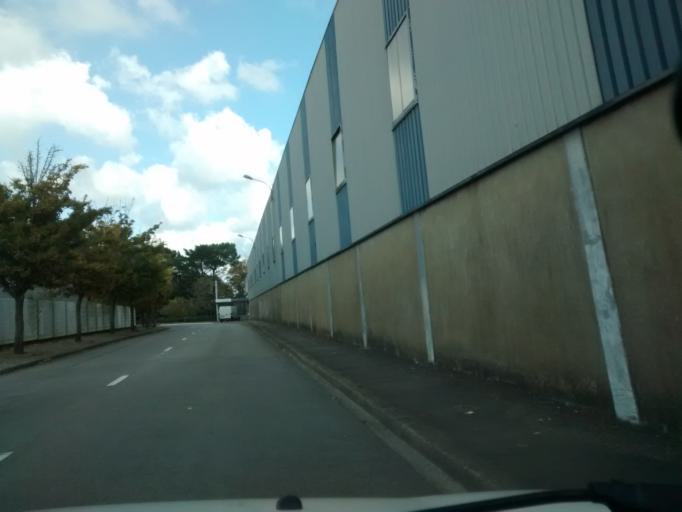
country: FR
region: Pays de la Loire
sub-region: Departement de la Loire-Atlantique
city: Saint-Paimboeuf
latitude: 47.2848
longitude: -2.0165
